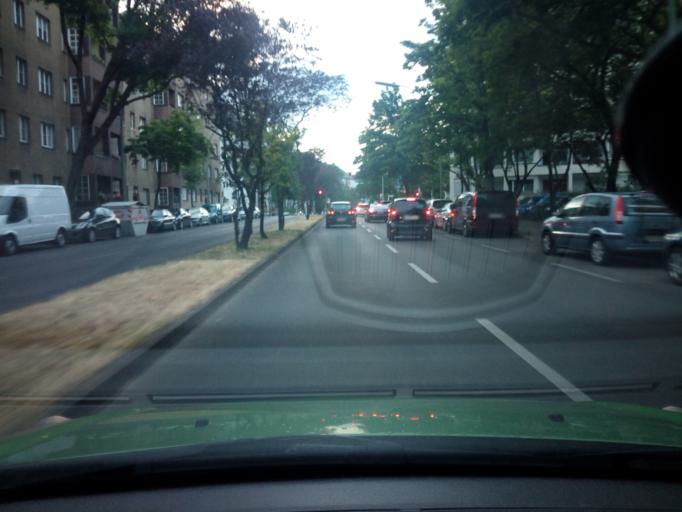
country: DE
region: Berlin
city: Tempelhof Bezirk
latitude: 52.4826
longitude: 13.3775
